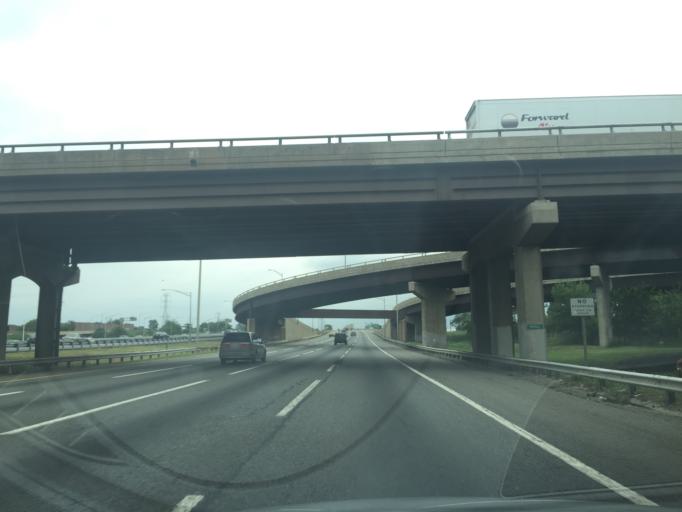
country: US
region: New Jersey
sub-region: Middlesex County
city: Carteret
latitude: 40.5945
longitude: -74.2340
